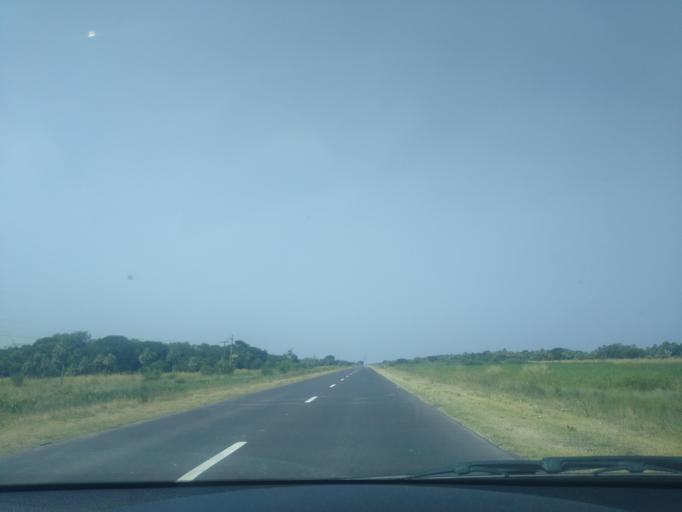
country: AR
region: Chaco
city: Fontana
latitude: -27.5549
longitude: -59.1454
